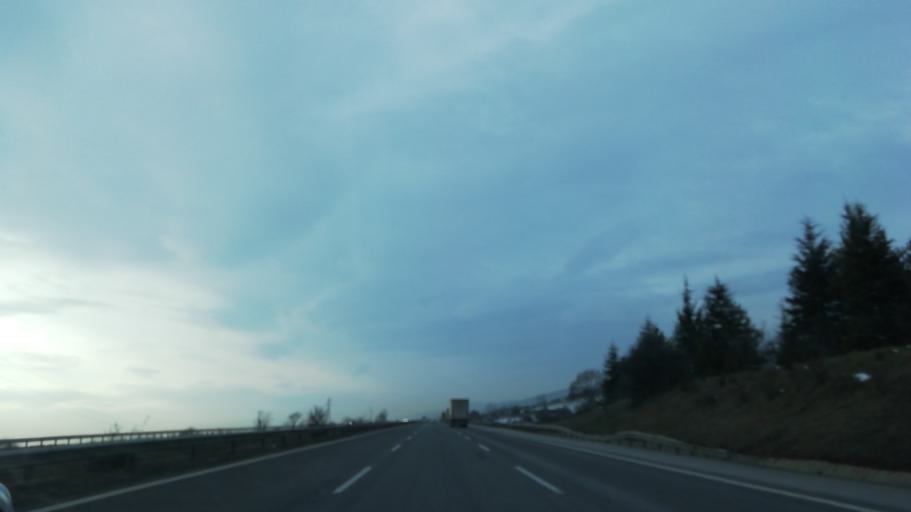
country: TR
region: Bolu
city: Bolu
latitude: 40.7649
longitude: 31.6215
